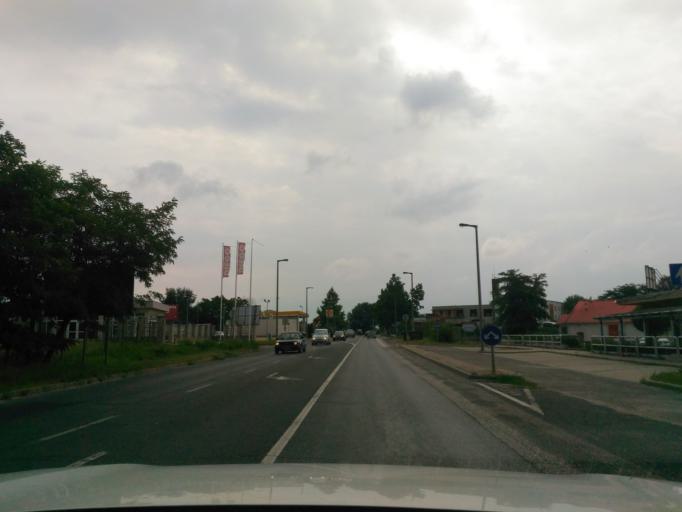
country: HU
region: Pest
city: Dabas
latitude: 47.1932
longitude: 19.3272
